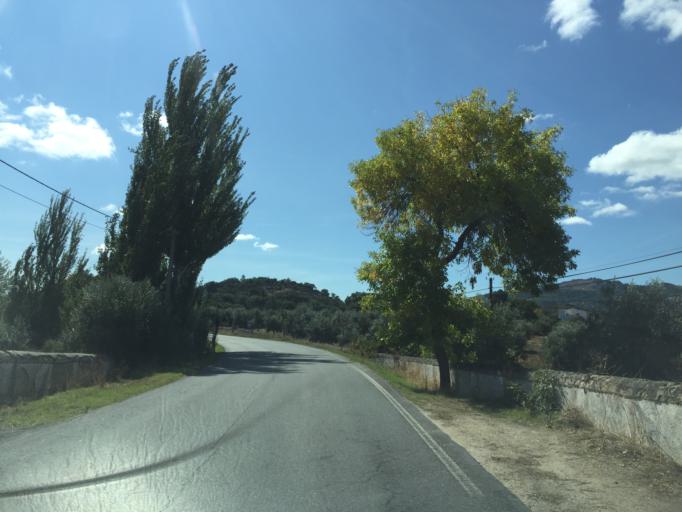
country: PT
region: Portalegre
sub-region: Marvao
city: Marvao
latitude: 39.4371
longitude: -7.3651
